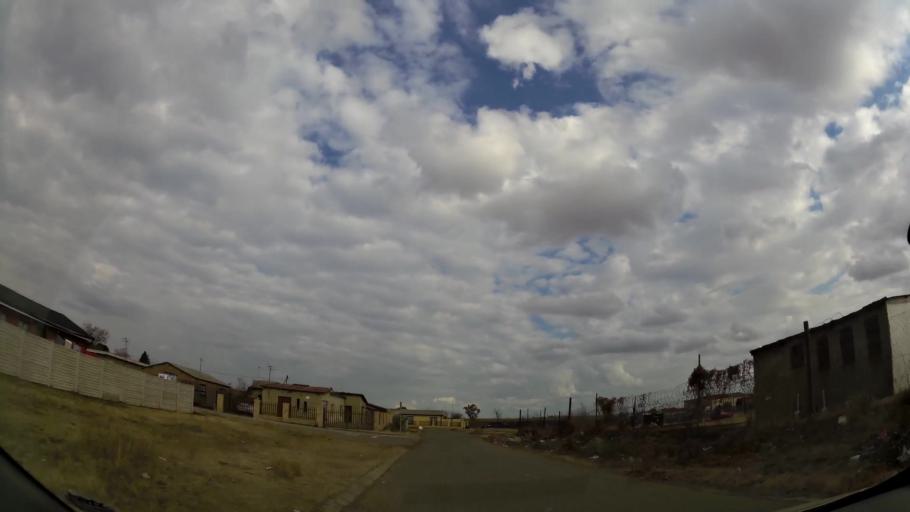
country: ZA
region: Orange Free State
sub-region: Fezile Dabi District Municipality
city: Sasolburg
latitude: -26.8416
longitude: 27.8437
